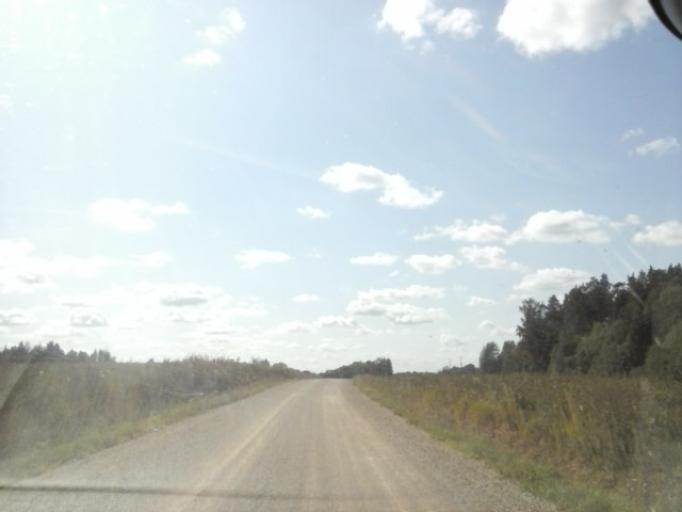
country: EE
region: Polvamaa
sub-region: Polva linn
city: Polva
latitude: 58.1052
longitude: 26.8557
